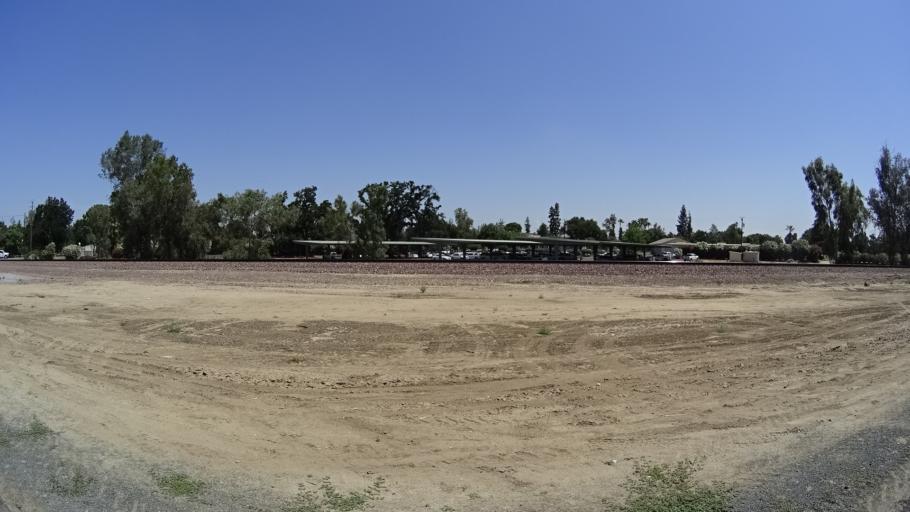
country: US
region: California
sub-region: Fresno County
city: Laton
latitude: 36.4219
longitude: -119.6742
